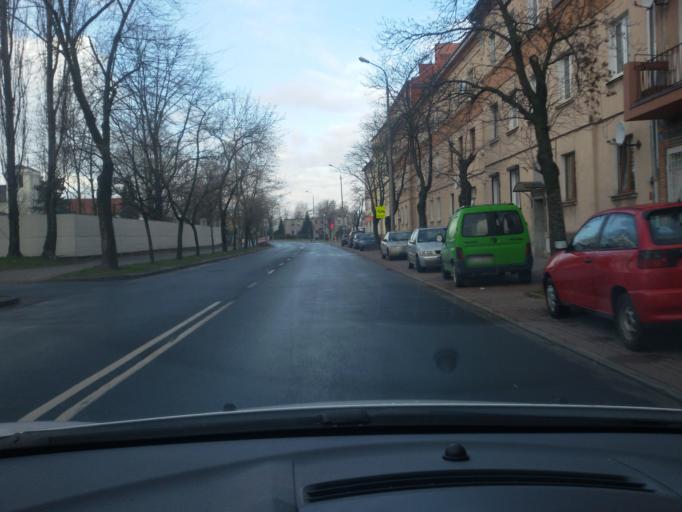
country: PL
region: Lower Silesian Voivodeship
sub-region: Powiat glogowski
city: Glogow
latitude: 51.6657
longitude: 16.0735
